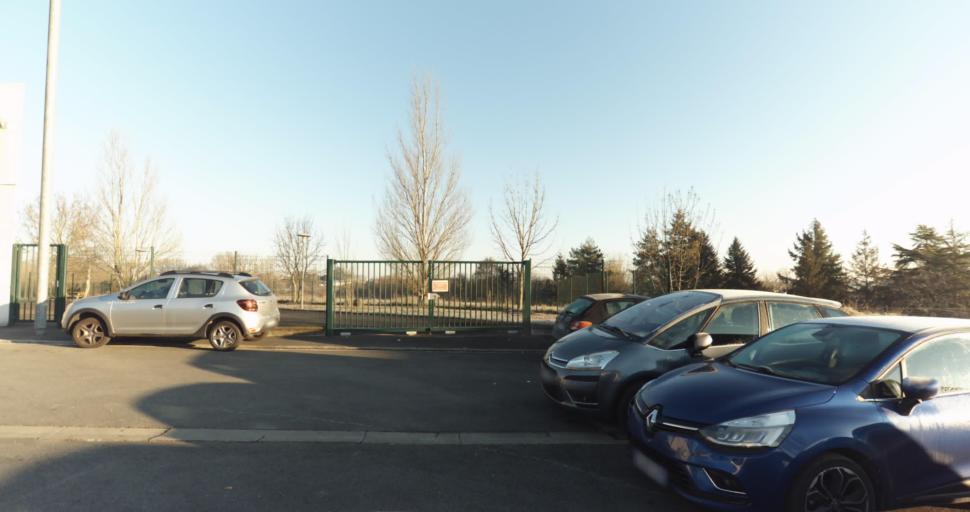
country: FR
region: Aquitaine
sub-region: Departement de la Gironde
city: Carbon-Blanc
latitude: 44.9107
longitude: -0.4991
